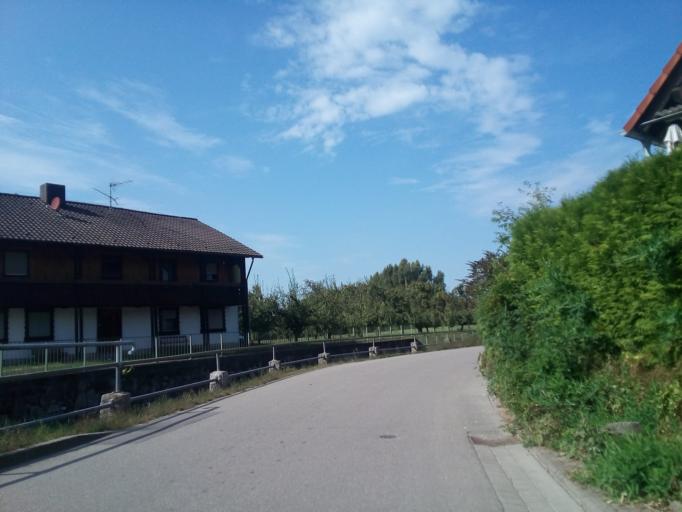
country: DE
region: Baden-Wuerttemberg
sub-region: Karlsruhe Region
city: Ottersweier
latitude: 48.6695
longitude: 8.1056
